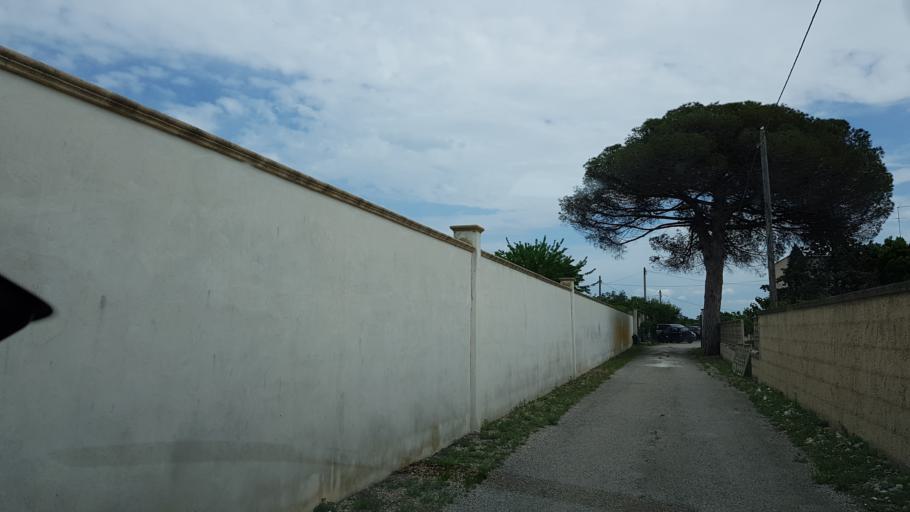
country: IT
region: Apulia
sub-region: Provincia di Brindisi
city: Brindisi
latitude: 40.6543
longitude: 17.9273
